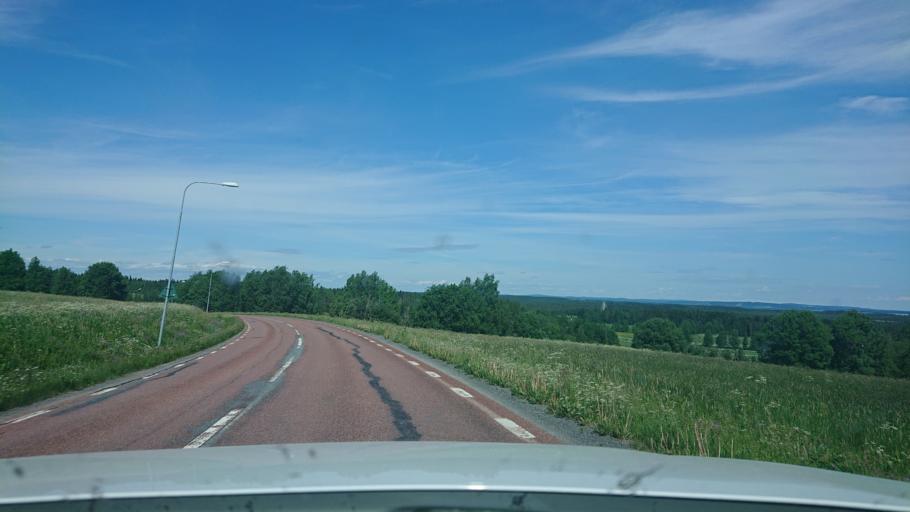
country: SE
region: Jaemtland
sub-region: Stroemsunds Kommun
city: Stroemsund
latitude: 63.7335
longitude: 15.4894
